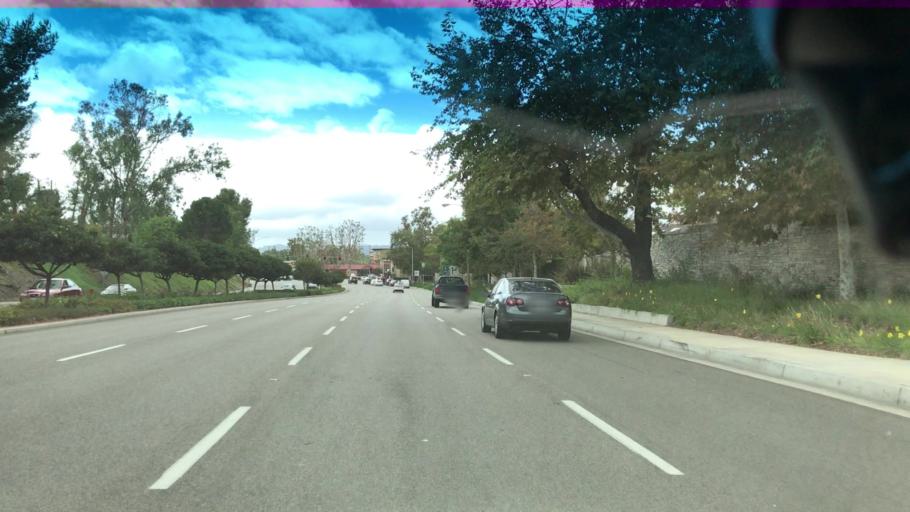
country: US
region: California
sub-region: Orange County
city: Mission Viejo
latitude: 33.6093
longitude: -117.6874
